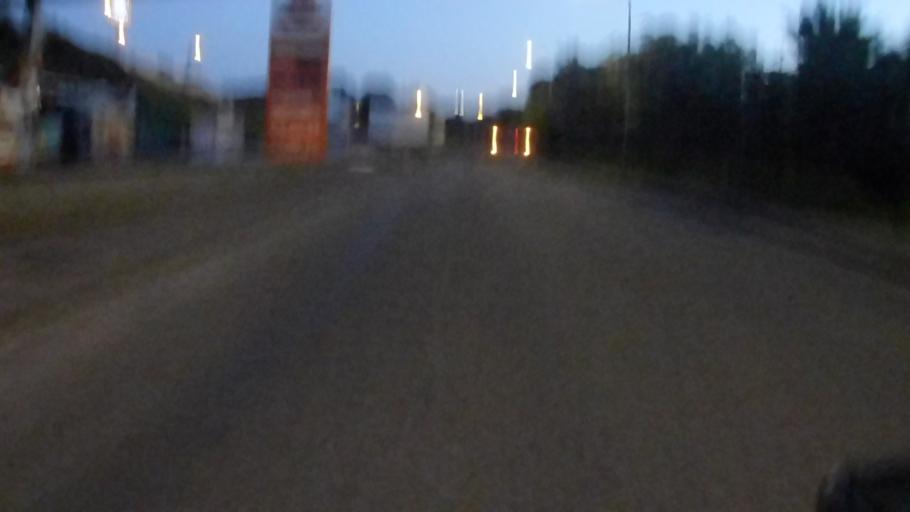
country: IE
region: Munster
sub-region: County Cork
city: Cork
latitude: 51.9158
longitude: -8.4271
